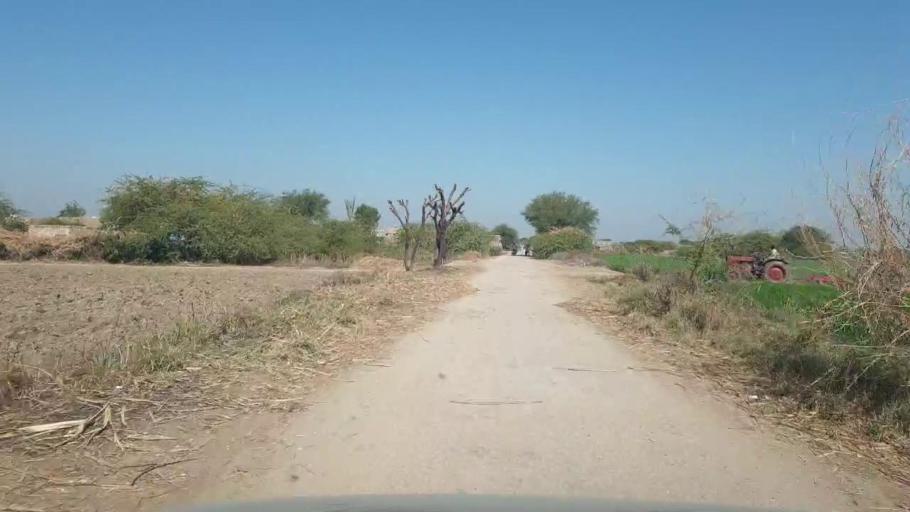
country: PK
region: Sindh
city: Mirwah Gorchani
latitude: 25.3094
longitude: 69.1044
